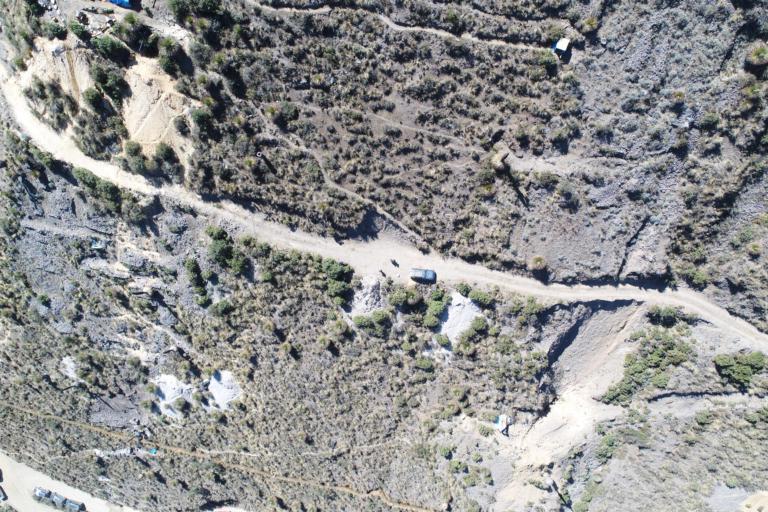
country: BO
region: La Paz
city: Viloco
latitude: -16.8137
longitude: -67.5520
